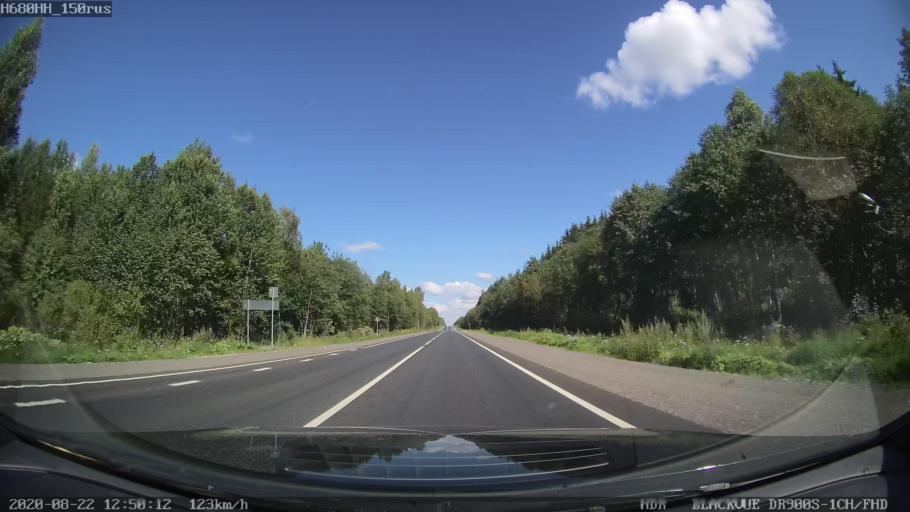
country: RU
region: Tverskaya
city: Rameshki
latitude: 57.4627
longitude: 36.2190
